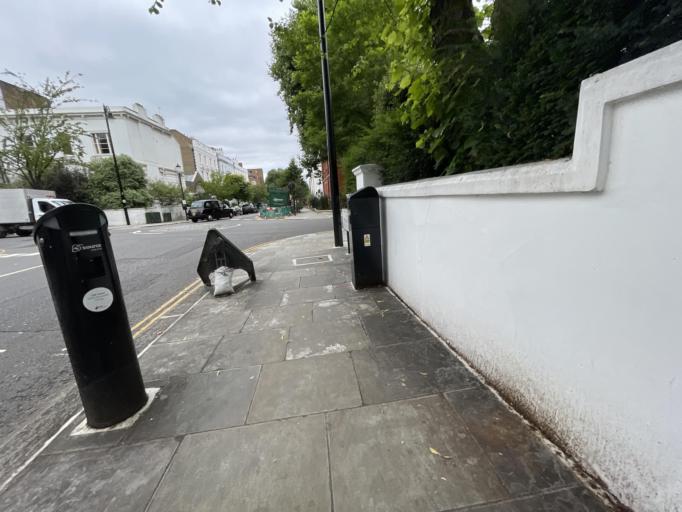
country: GB
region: England
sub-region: Greater London
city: Kensington
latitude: 51.5128
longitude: -0.2000
